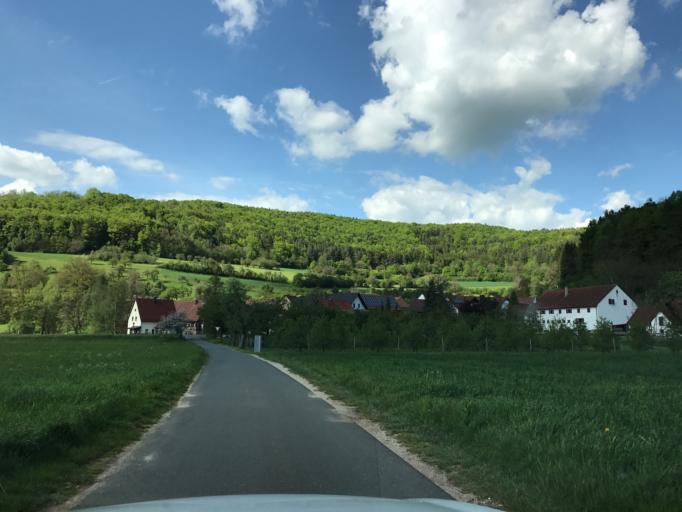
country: DE
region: Bavaria
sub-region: Upper Franconia
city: Egloffstein
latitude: 49.7283
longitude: 11.2429
